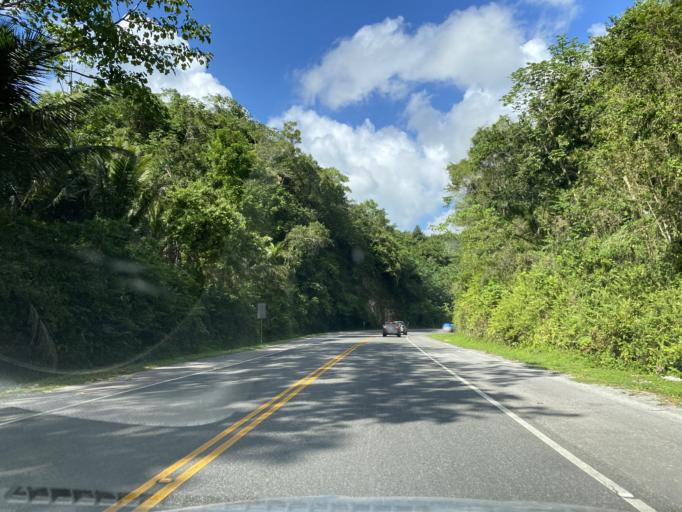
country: DO
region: Monte Plata
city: Majagual
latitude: 19.0904
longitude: -69.8330
